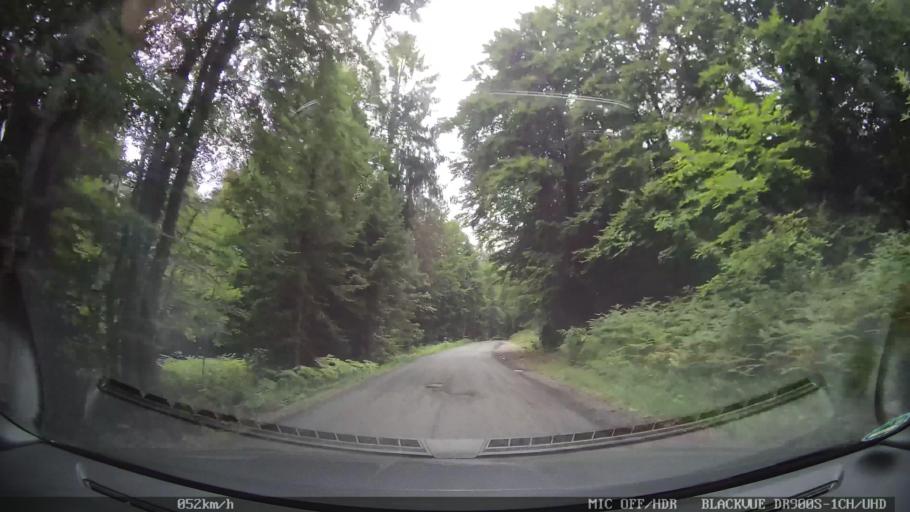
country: HR
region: Licko-Senjska
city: Jezerce
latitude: 44.9264
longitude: 15.5695
